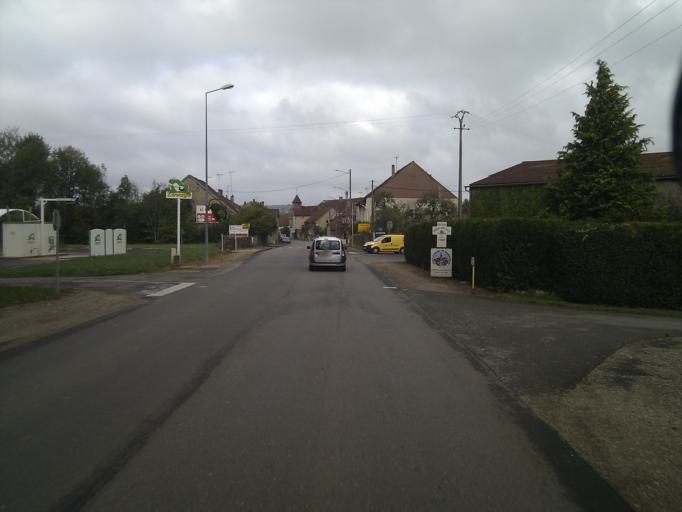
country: FR
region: Lorraine
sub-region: Departement des Vosges
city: Liffol-le-Grand
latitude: 48.3178
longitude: 5.5889
